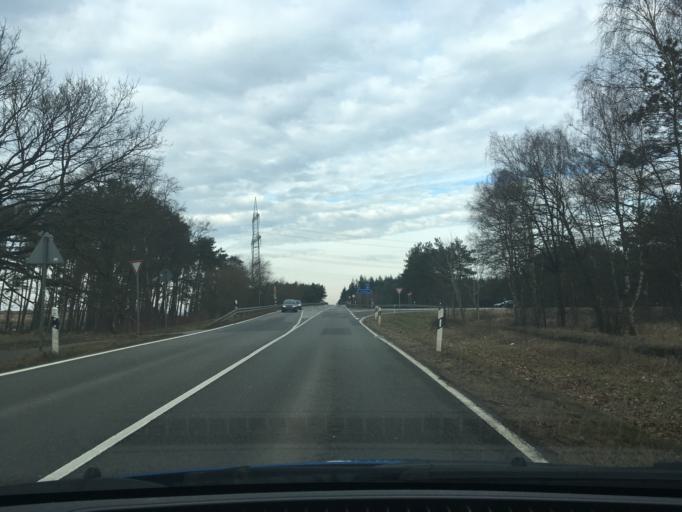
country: DE
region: Mecklenburg-Vorpommern
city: Zarrentin
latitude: 53.5094
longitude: 10.8930
